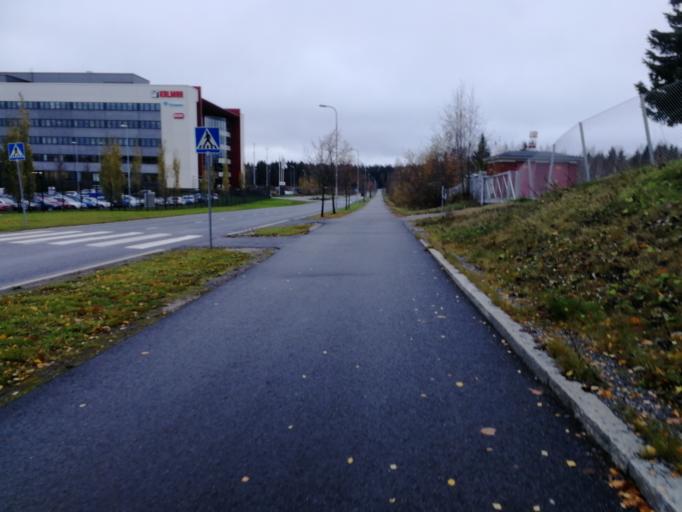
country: FI
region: Pirkanmaa
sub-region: Tampere
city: Tampere
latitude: 61.4522
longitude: 23.9007
